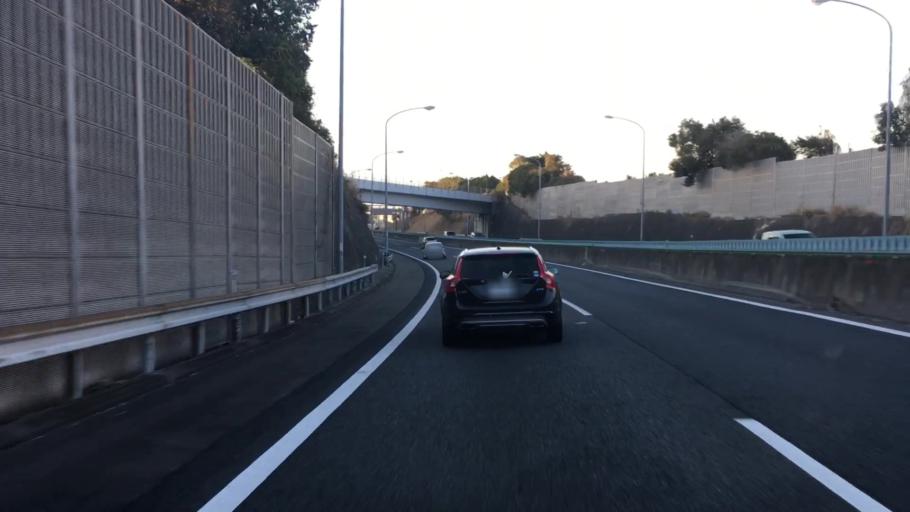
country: JP
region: Kanagawa
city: Kamakura
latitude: 35.3710
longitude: 139.5935
